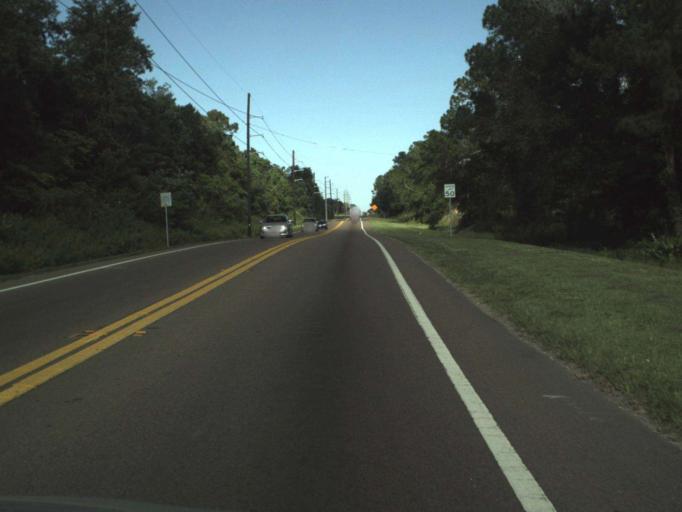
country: US
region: Florida
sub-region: Seminole County
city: Midway
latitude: 28.7868
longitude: -81.2509
